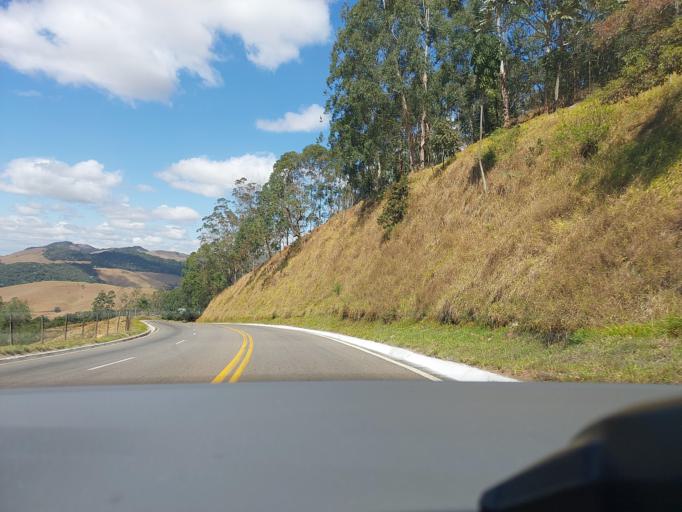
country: BR
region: Minas Gerais
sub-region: Mirai
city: Mirai
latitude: -21.0399
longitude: -42.5330
